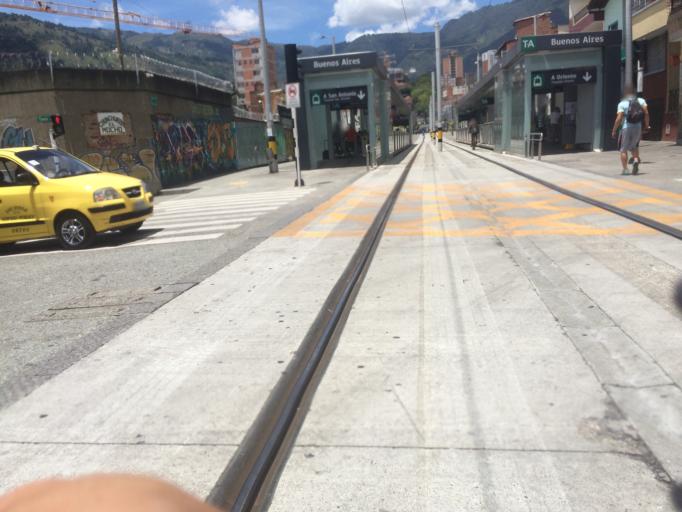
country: CO
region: Antioquia
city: Medellin
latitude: 6.2417
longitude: -75.5544
